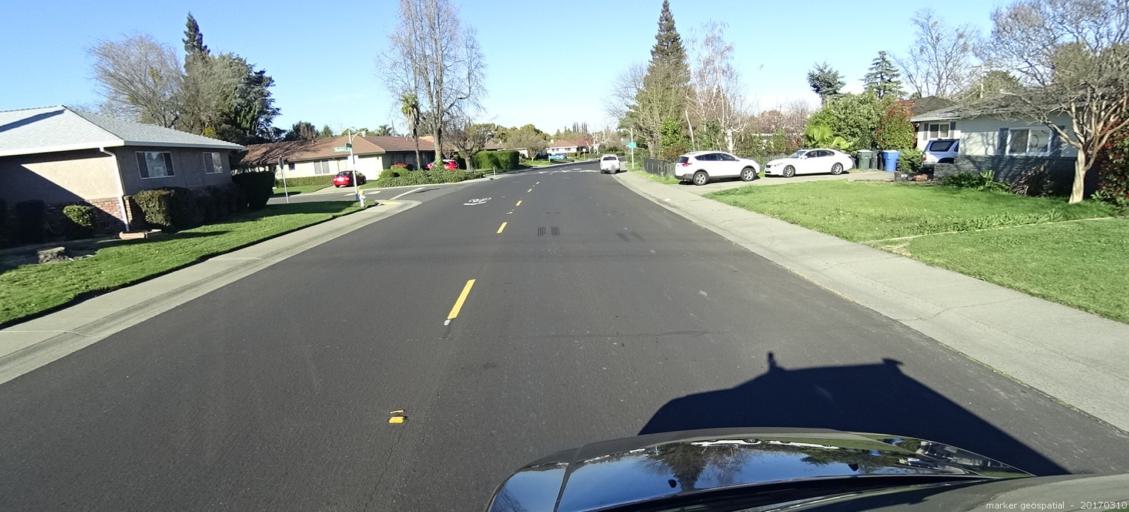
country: US
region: California
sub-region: Yolo County
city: West Sacramento
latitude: 38.5184
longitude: -121.5184
